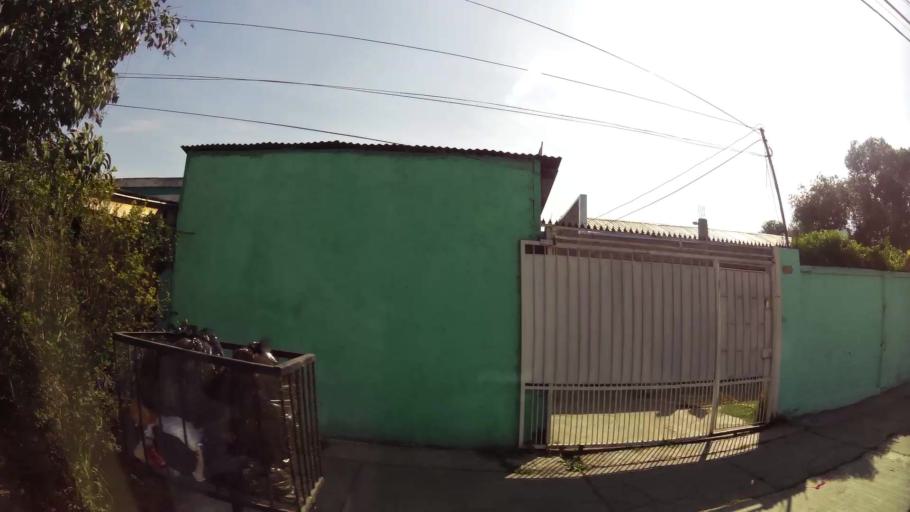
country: CL
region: Santiago Metropolitan
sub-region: Provincia de Santiago
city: La Pintana
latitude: -33.5627
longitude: -70.6674
